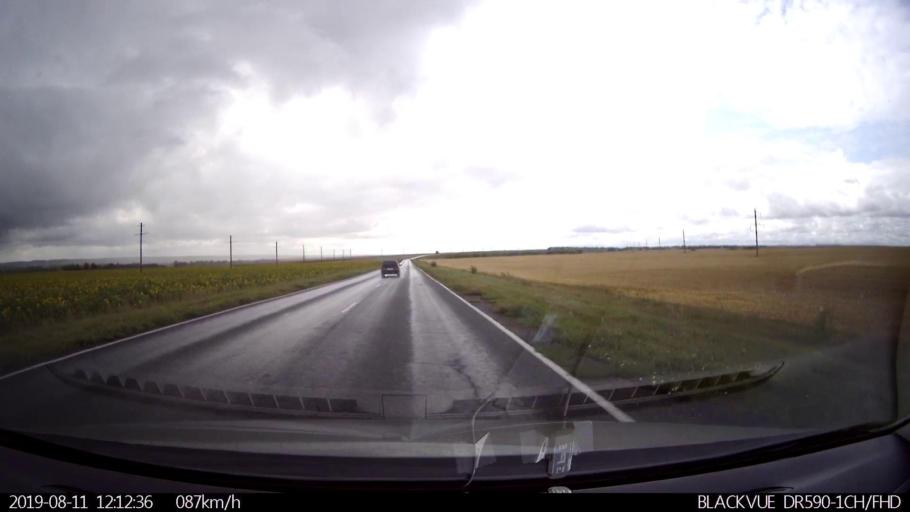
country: RU
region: Ulyanovsk
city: Silikatnyy
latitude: 53.9710
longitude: 47.9959
